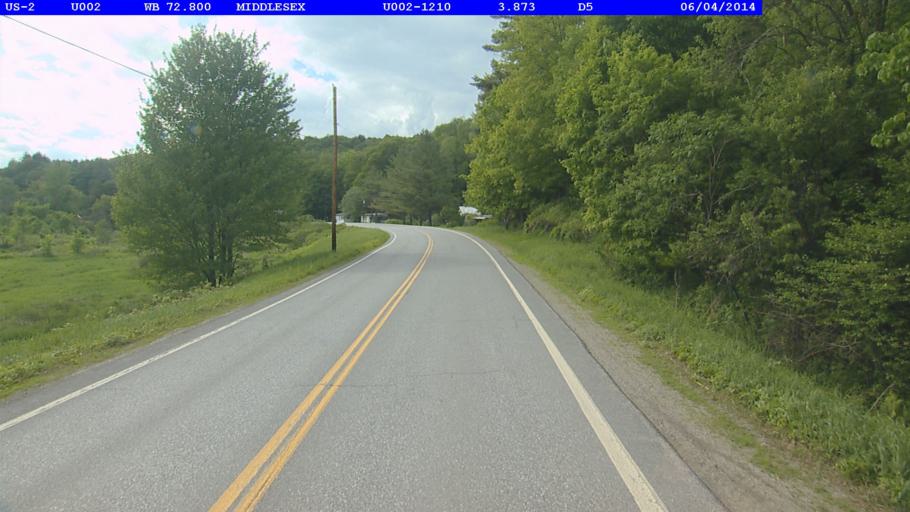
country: US
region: Vermont
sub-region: Washington County
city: Montpelier
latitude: 44.2746
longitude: -72.6399
